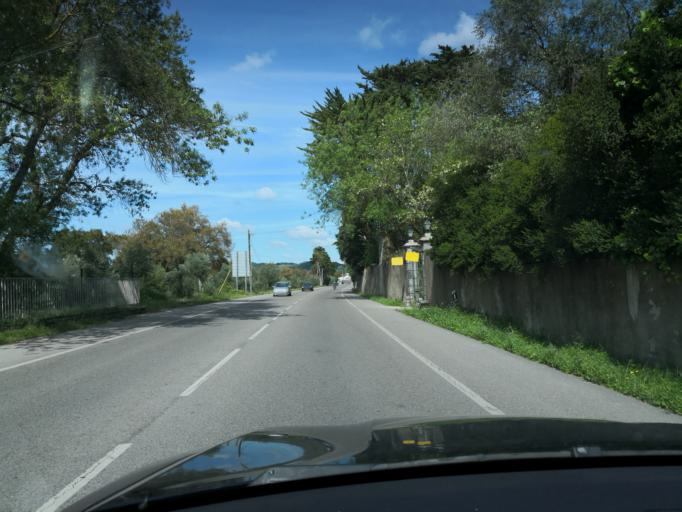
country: PT
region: Setubal
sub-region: Palmela
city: Quinta do Anjo
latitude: 38.5219
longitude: -9.0069
